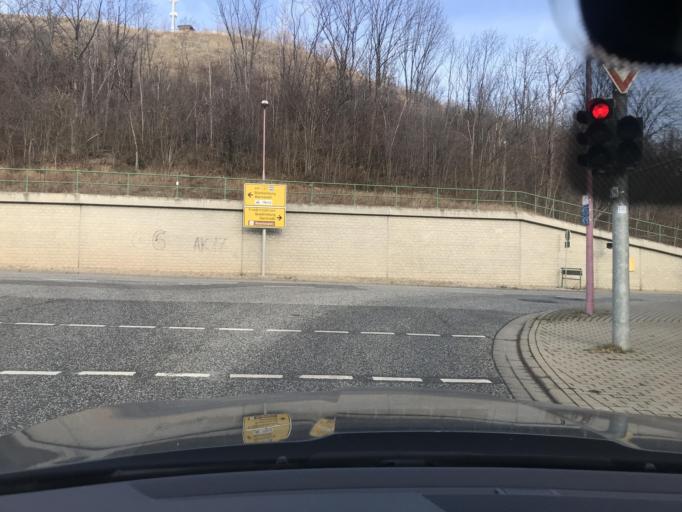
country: DE
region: Saxony-Anhalt
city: Thale
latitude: 51.7579
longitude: 11.0369
